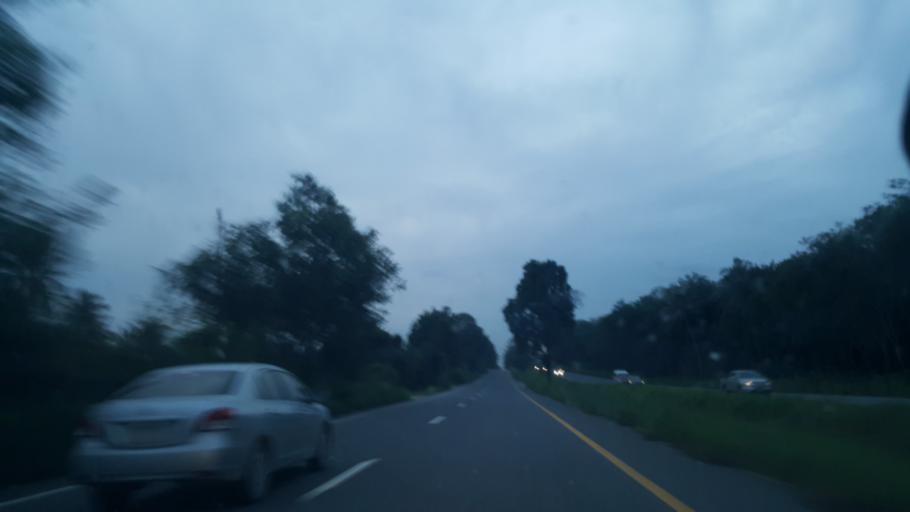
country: TH
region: Rayong
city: Ban Chang
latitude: 12.7885
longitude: 100.9920
